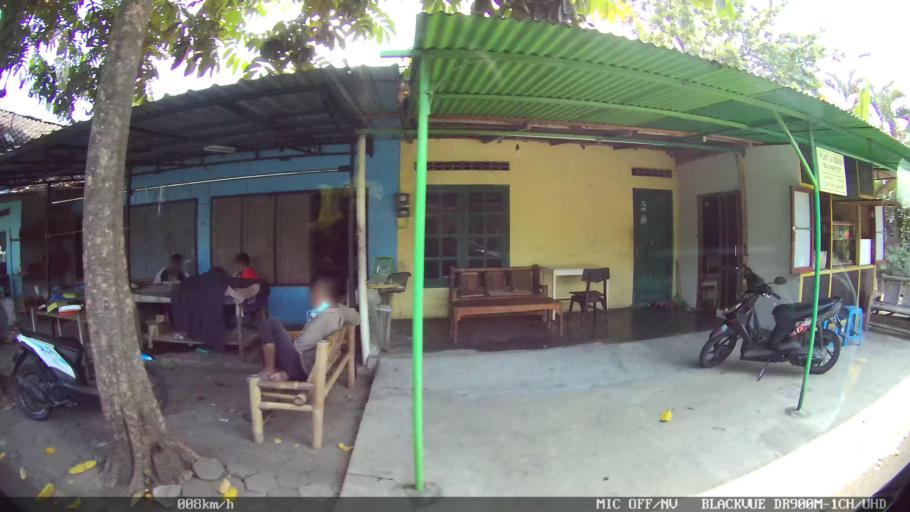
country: ID
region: Daerah Istimewa Yogyakarta
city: Yogyakarta
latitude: -7.8168
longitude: 110.3969
